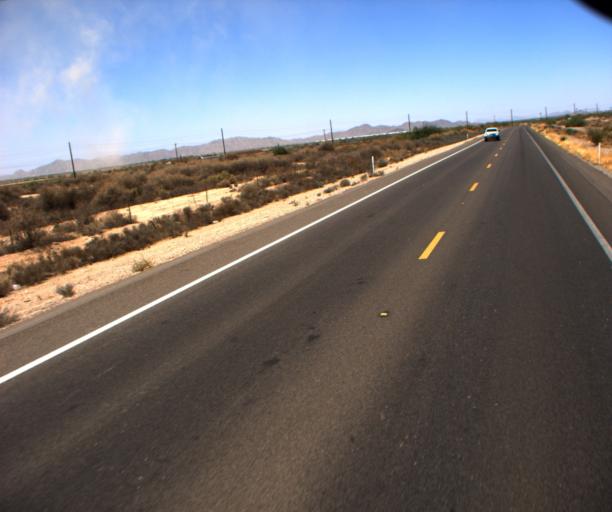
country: US
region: Arizona
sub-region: Pinal County
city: Maricopa
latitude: 33.0723
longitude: -112.0719
